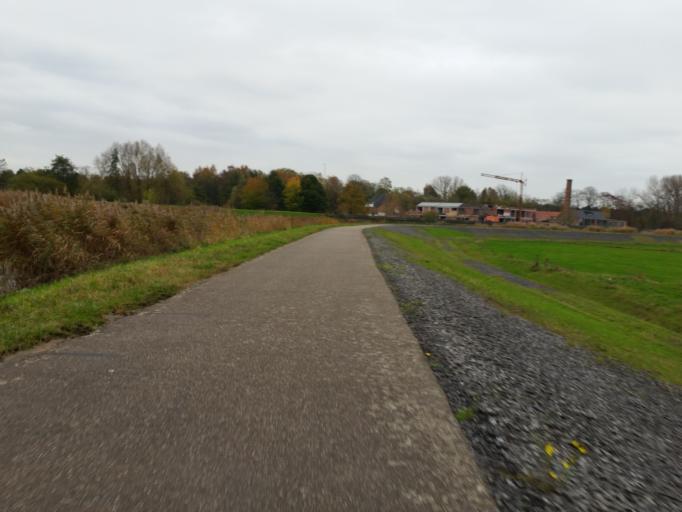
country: BE
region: Flanders
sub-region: Provincie Antwerpen
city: Lier
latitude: 51.1206
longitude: 4.5599
